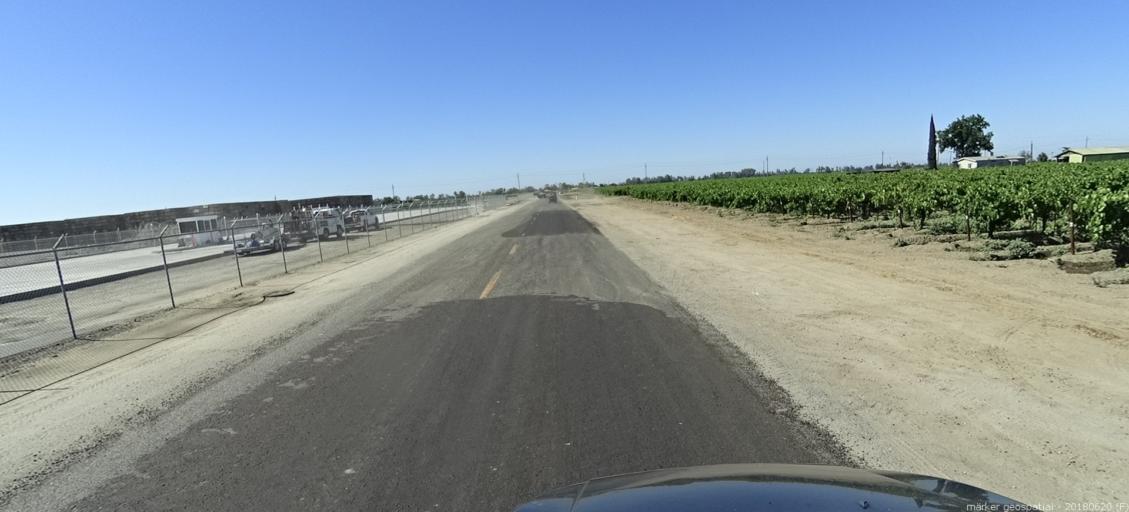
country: US
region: California
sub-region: Madera County
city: Parkwood
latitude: 36.9191
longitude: -120.0466
